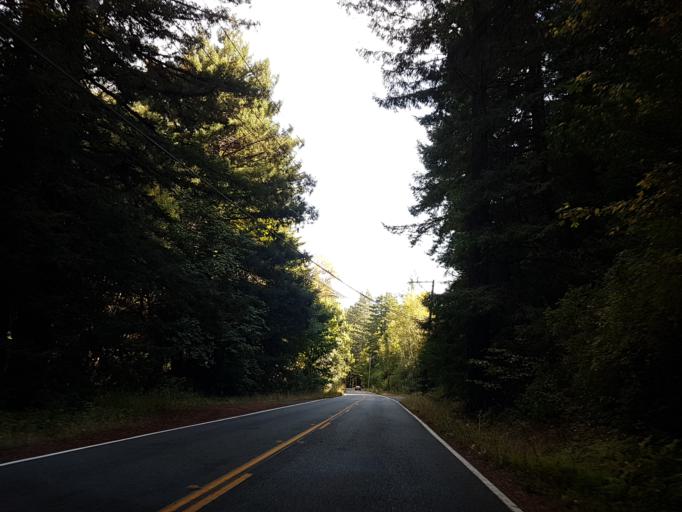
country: US
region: California
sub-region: Humboldt County
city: Rio Dell
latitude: 40.4133
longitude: -123.9601
